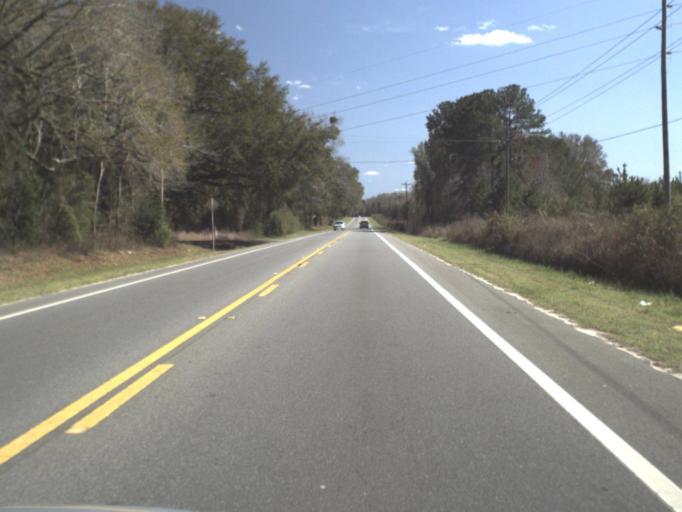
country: US
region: Florida
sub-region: Gadsden County
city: Gretna
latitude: 30.6029
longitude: -84.6532
